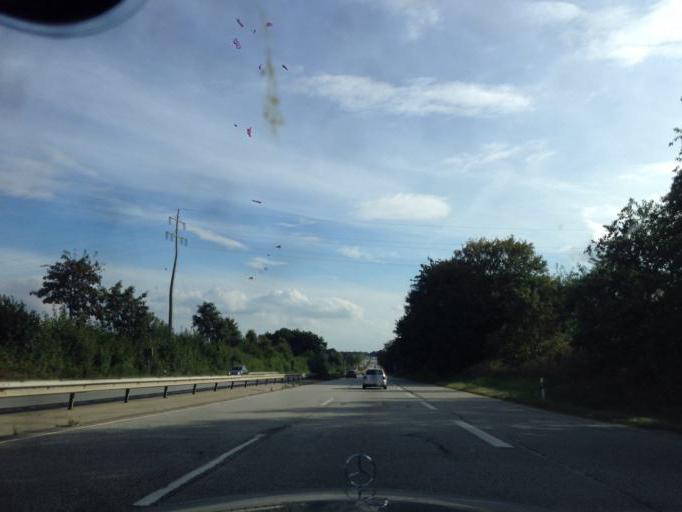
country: DE
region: Schleswig-Holstein
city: Hogersdorf
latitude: 53.9172
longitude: 10.2738
